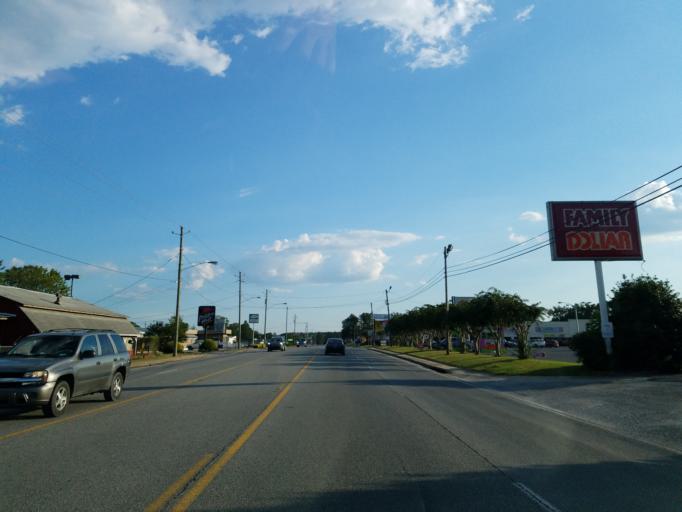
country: US
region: Georgia
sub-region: Murray County
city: Chatsworth
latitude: 34.7622
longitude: -84.7696
